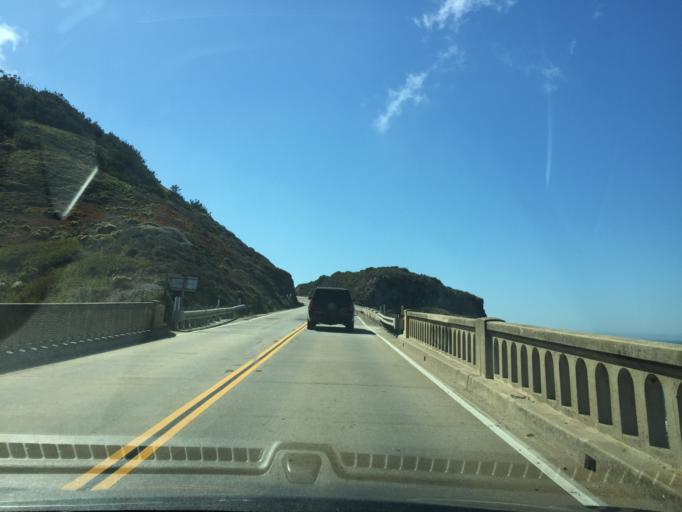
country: US
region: California
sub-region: Monterey County
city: Carmel-by-the-Sea
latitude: 36.3790
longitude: -121.9029
